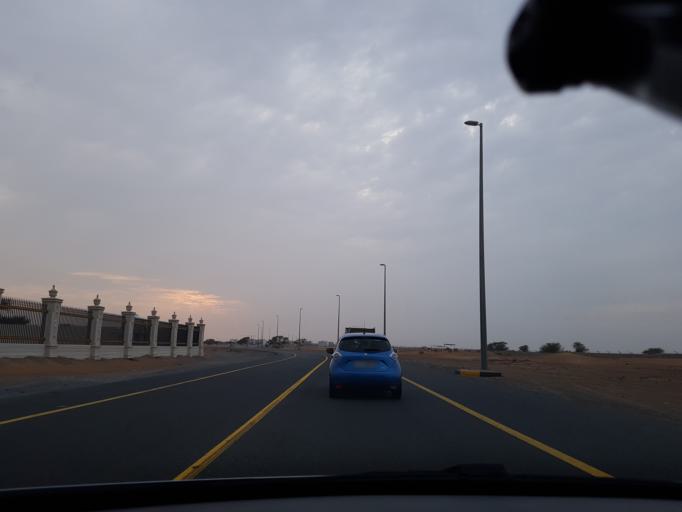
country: AE
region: Ash Shariqah
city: Adh Dhayd
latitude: 25.2697
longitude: 55.9094
